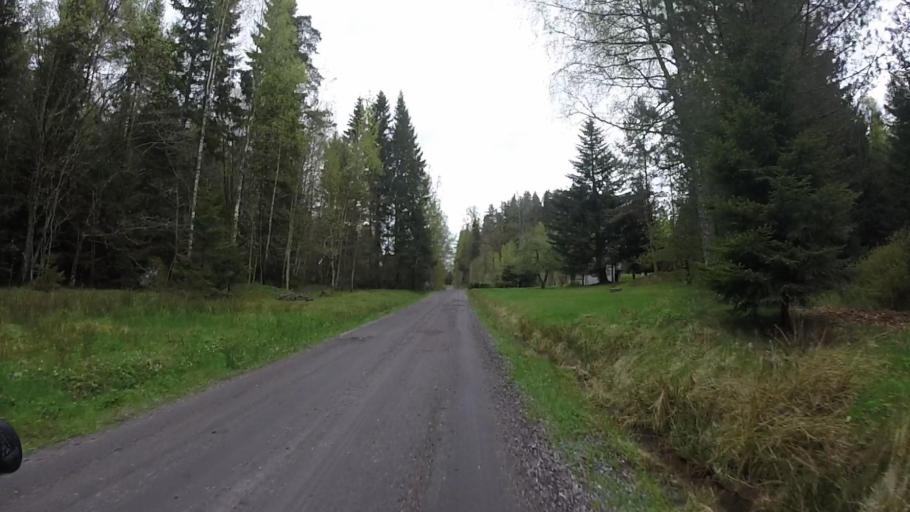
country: SE
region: Vaestra Goetaland
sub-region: Trollhattan
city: Sjuntorp
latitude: 58.2086
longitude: 12.2113
